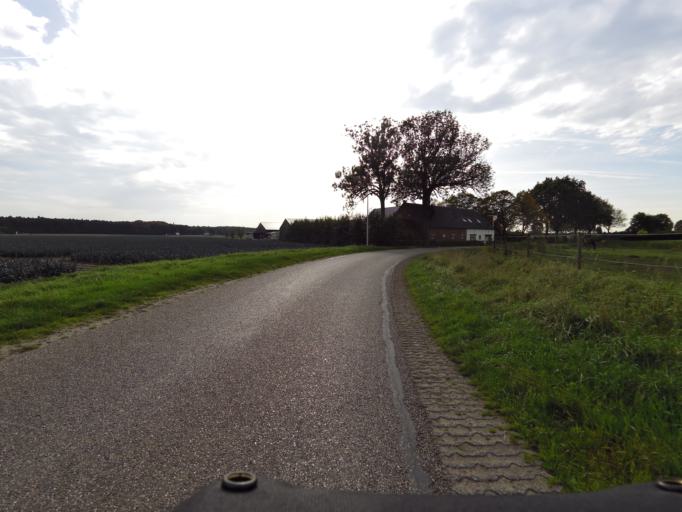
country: NL
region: North Brabant
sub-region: Gemeente Woensdrecht
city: Woensdrecht
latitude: 51.3836
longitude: 4.3375
